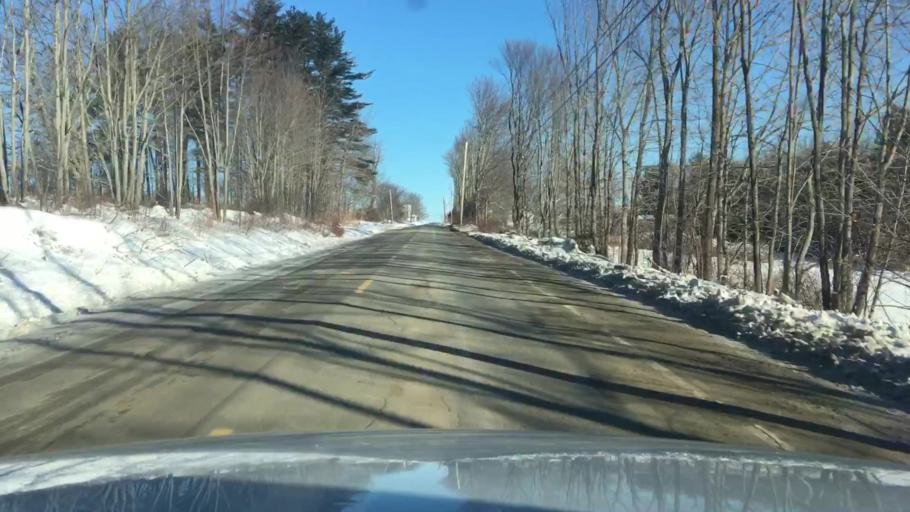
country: US
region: Maine
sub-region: Kennebec County
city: Mount Vernon
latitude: 44.4790
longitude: -69.9725
